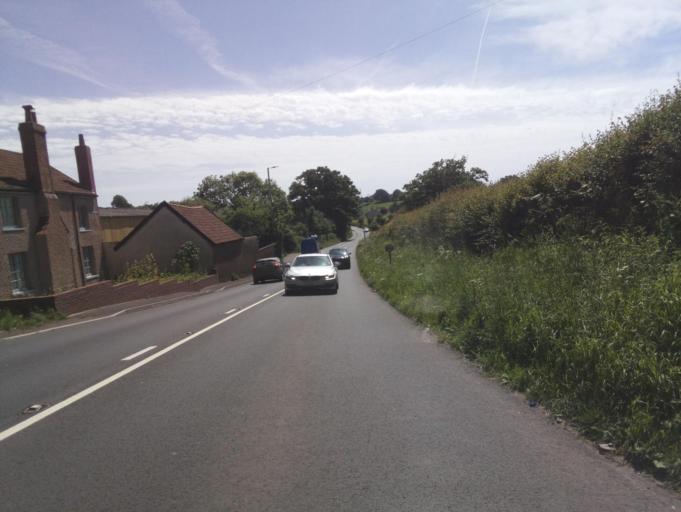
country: GB
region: England
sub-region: Devon
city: Starcross
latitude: 50.6525
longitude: -3.4186
